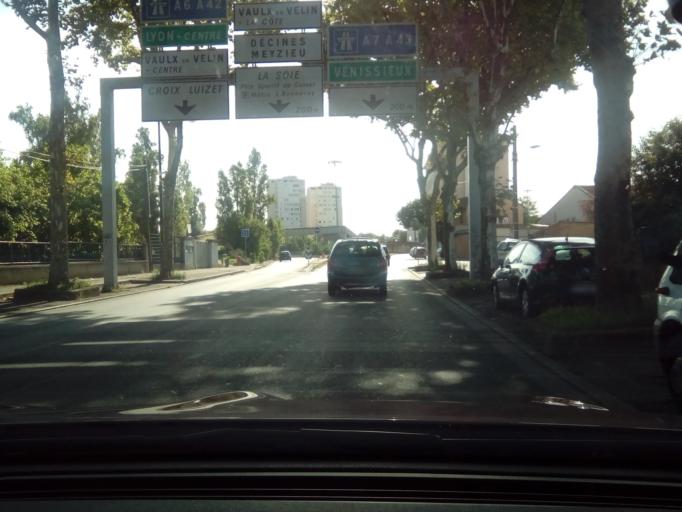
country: FR
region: Rhone-Alpes
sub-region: Departement du Rhone
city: Villeurbanne
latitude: 45.7647
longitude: 4.9054
